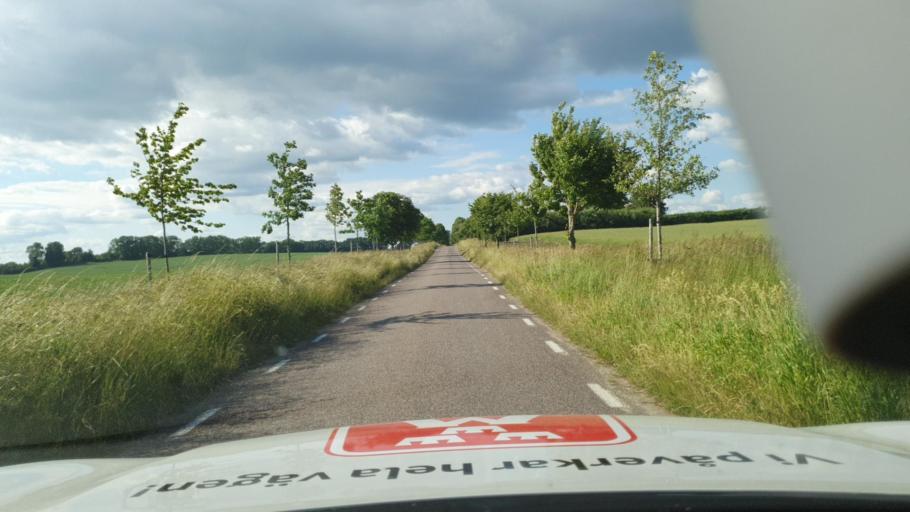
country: SE
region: Skane
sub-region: Ystads Kommun
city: Ystad
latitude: 55.4370
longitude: 13.7365
